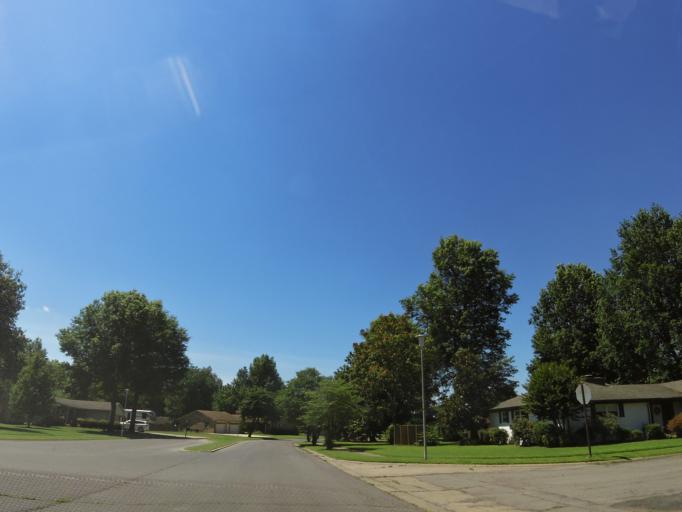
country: US
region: Missouri
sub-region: New Madrid County
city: New Madrid
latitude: 36.5978
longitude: -89.5267
